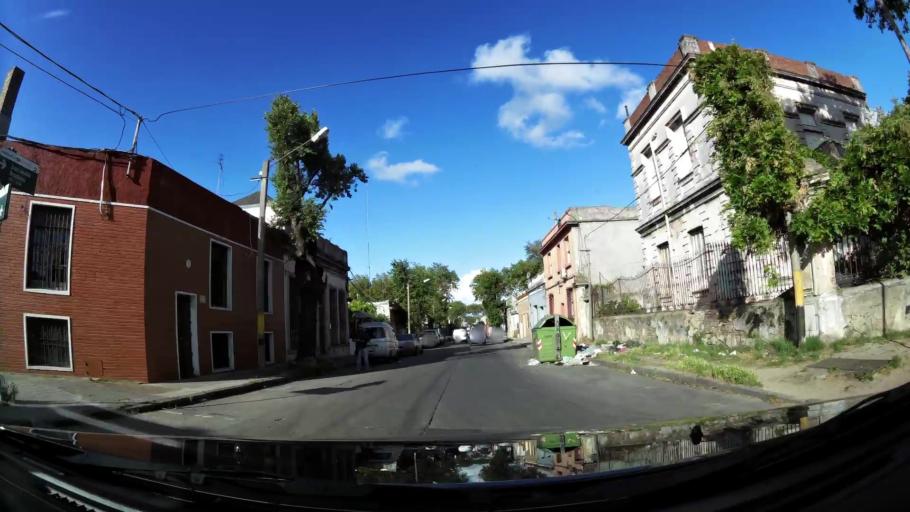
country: UY
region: Montevideo
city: Montevideo
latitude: -34.8741
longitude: -56.1428
